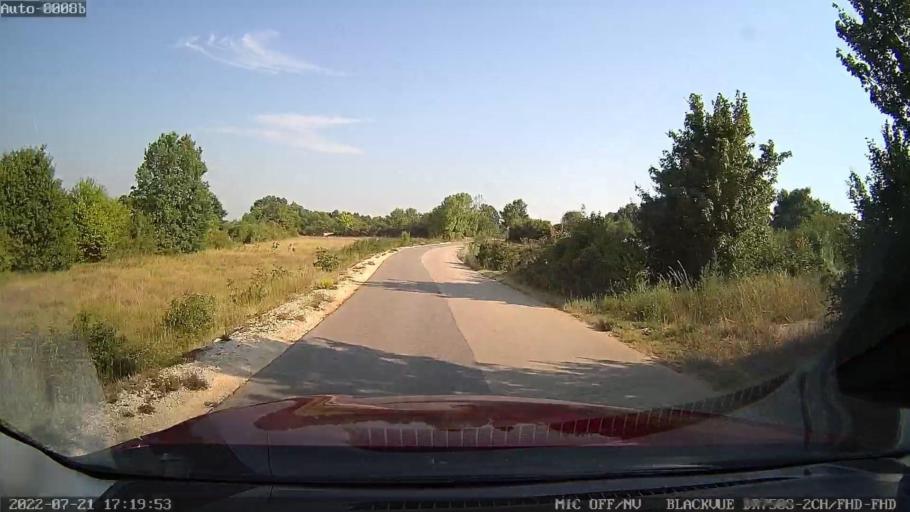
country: HR
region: Istarska
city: Karojba
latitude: 45.2086
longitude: 13.8276
